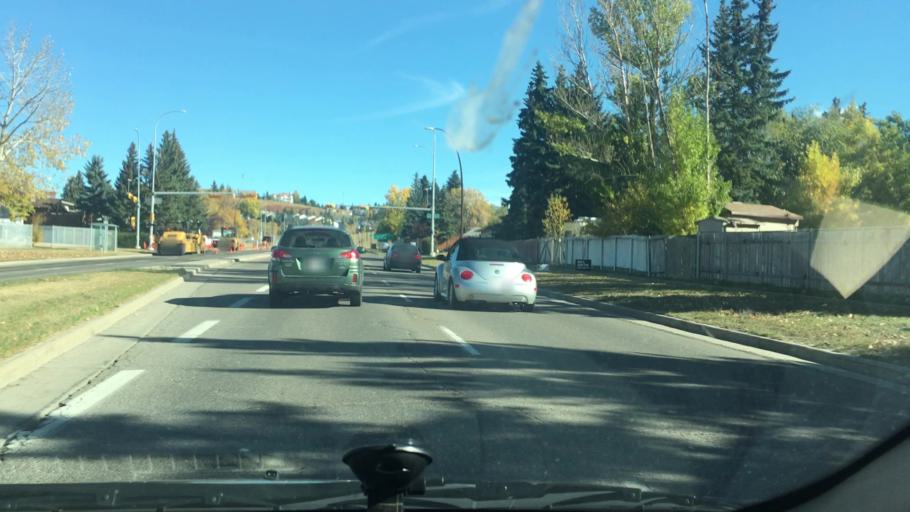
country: CA
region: Alberta
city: Calgary
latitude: 51.1126
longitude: -114.1571
